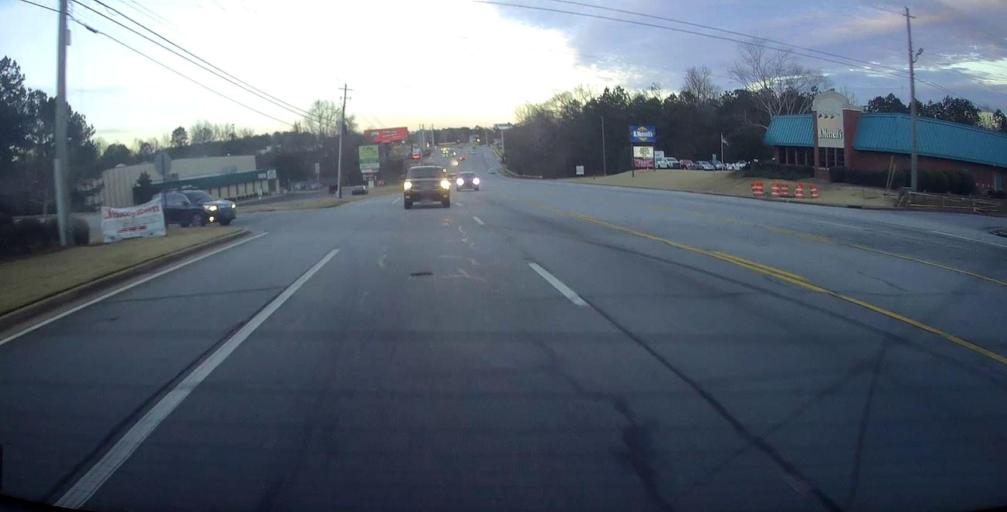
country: US
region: Alabama
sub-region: Russell County
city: Phenix City
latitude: 32.5576
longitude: -84.9436
